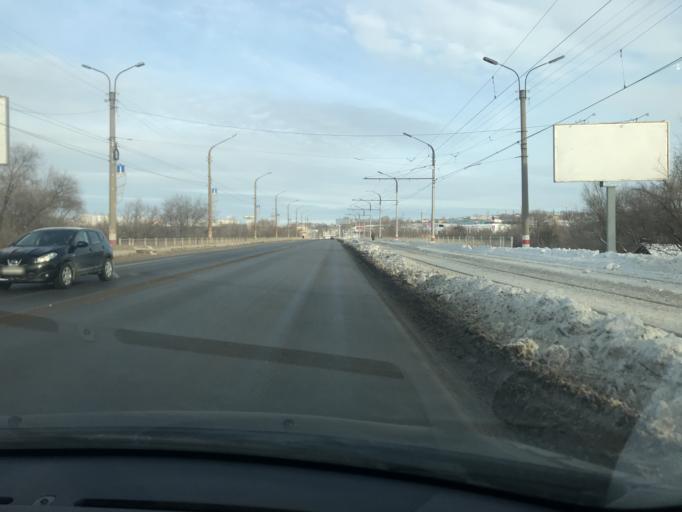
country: RU
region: Ulyanovsk
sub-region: Ulyanovskiy Rayon
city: Ulyanovsk
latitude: 54.3232
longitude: 48.3570
